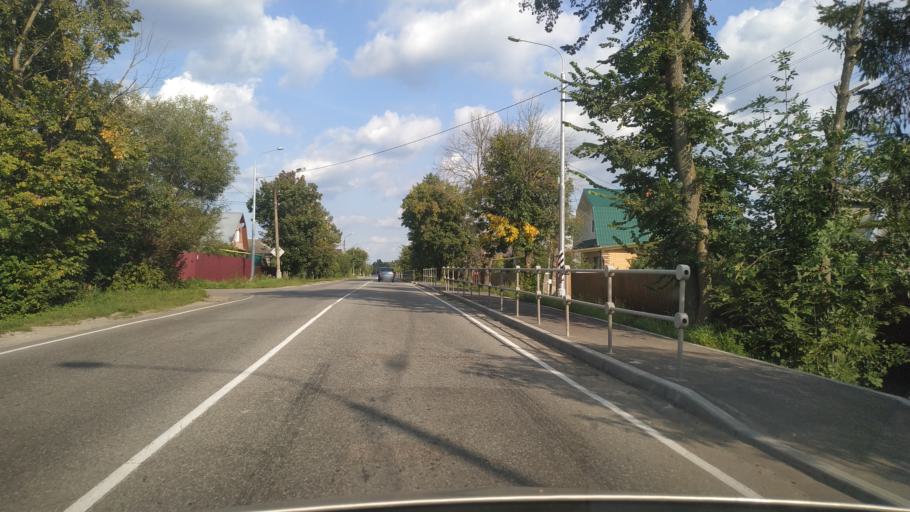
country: RU
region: Moskovskaya
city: Likino-Dulevo
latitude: 55.7301
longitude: 38.9961
